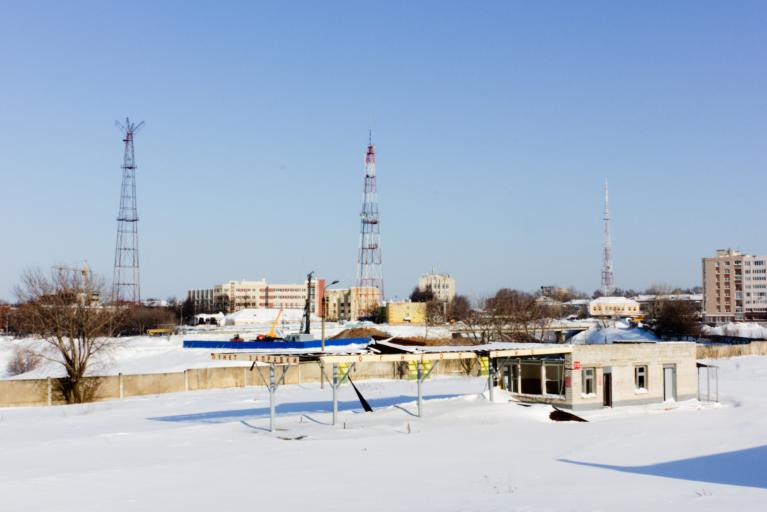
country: RU
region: Nizjnij Novgorod
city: Nizhniy Novgorod
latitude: 56.3028
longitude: 43.9730
